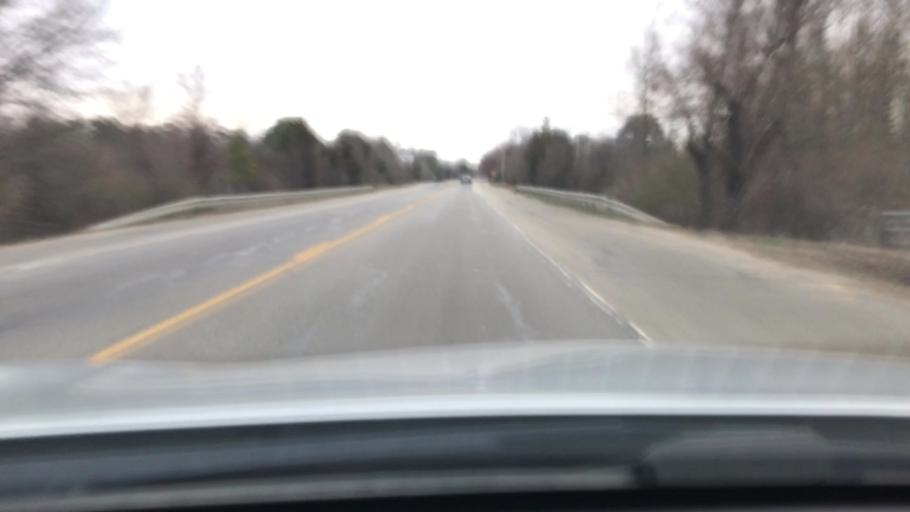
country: US
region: Arkansas
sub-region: Hempstead County
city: Hope
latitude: 33.6879
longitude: -93.5870
